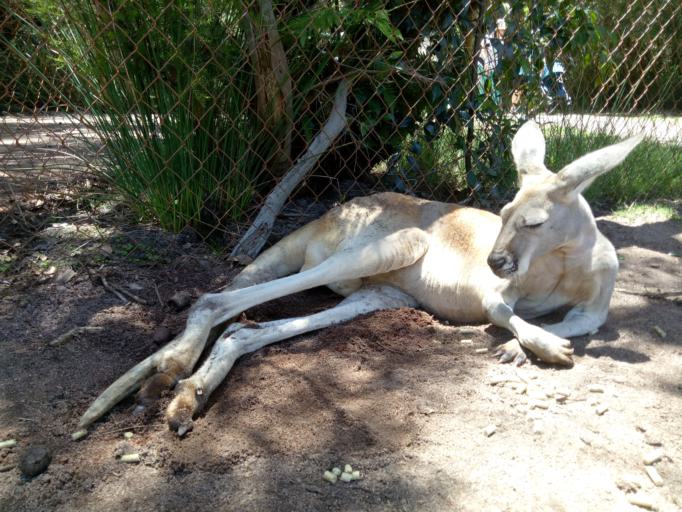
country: AU
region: Western Australia
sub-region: Swan
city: Henley Brook
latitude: -31.8336
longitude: 115.9509
